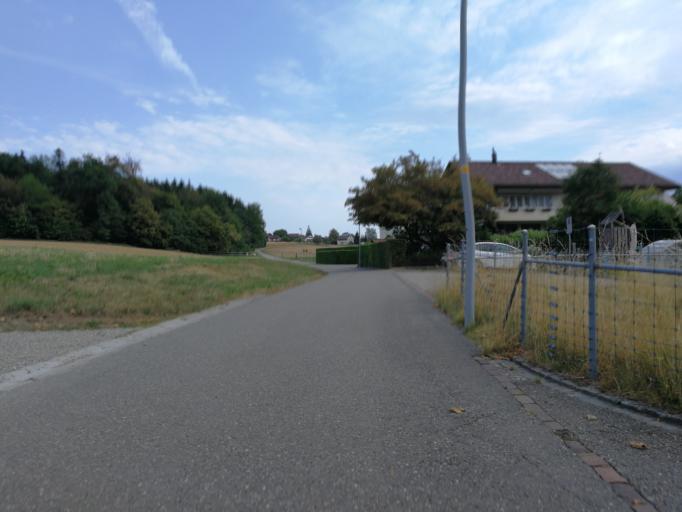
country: CH
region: Zurich
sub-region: Bezirk Hinwil
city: Wetzikon / Robenhausen
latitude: 47.3388
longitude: 8.7686
